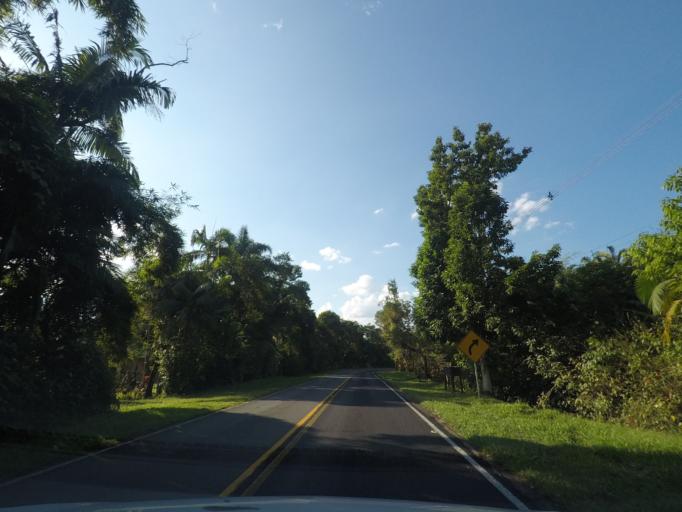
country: BR
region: Parana
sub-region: Antonina
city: Antonina
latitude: -25.4207
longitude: -48.8751
